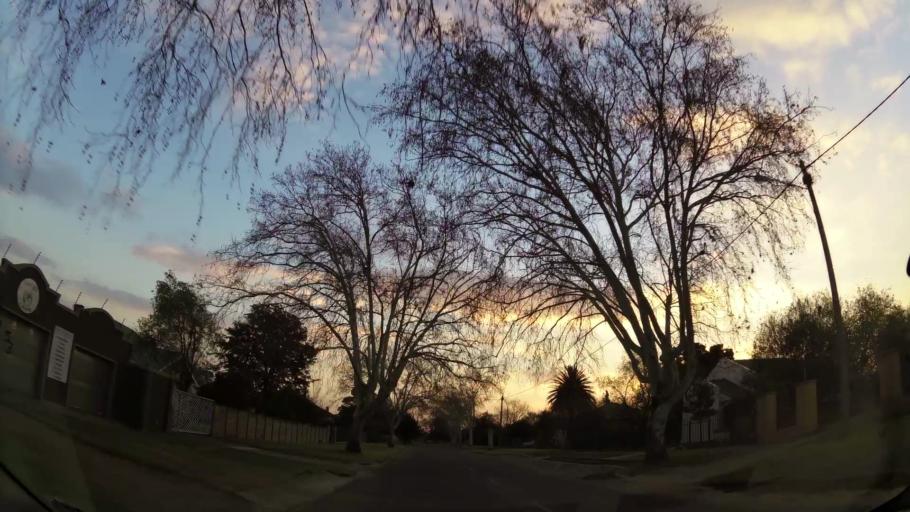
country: ZA
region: Gauteng
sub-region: Ekurhuleni Metropolitan Municipality
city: Benoni
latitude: -26.1724
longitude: 28.3202
